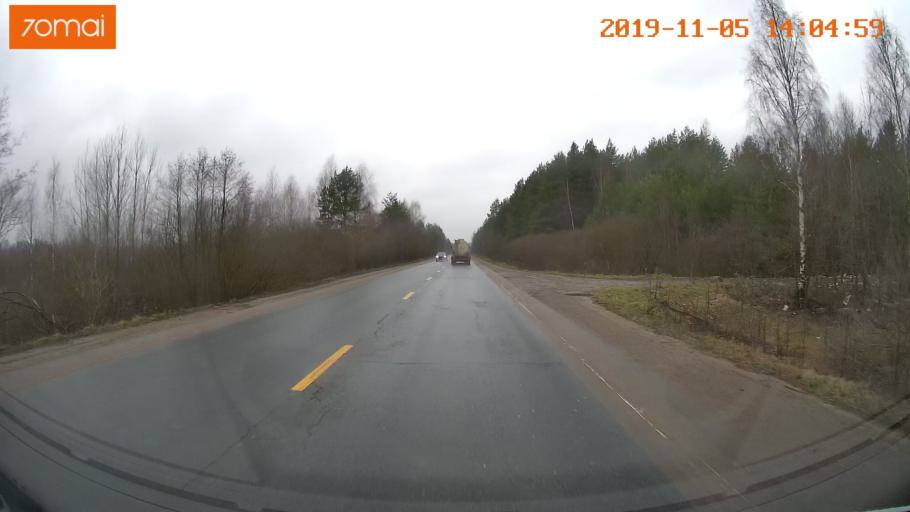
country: RU
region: Ivanovo
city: Kokhma
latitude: 56.9975
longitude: 41.1658
